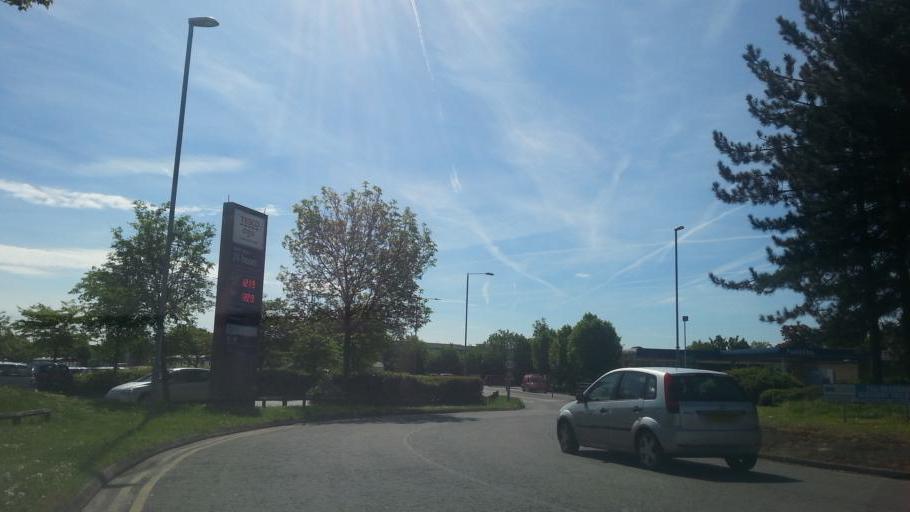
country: GB
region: England
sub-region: Cambridgeshire
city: Huntingdon
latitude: 52.3526
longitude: -0.1817
